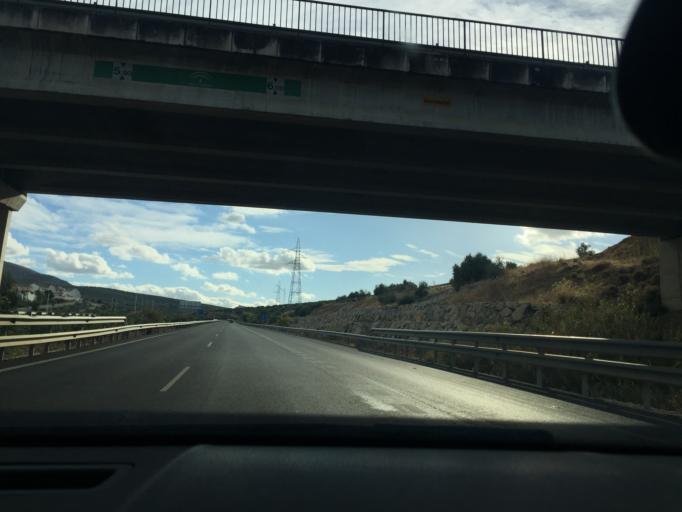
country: ES
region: Andalusia
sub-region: Provincia de Jaen
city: Torre del Campo
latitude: 37.7772
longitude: -3.9034
